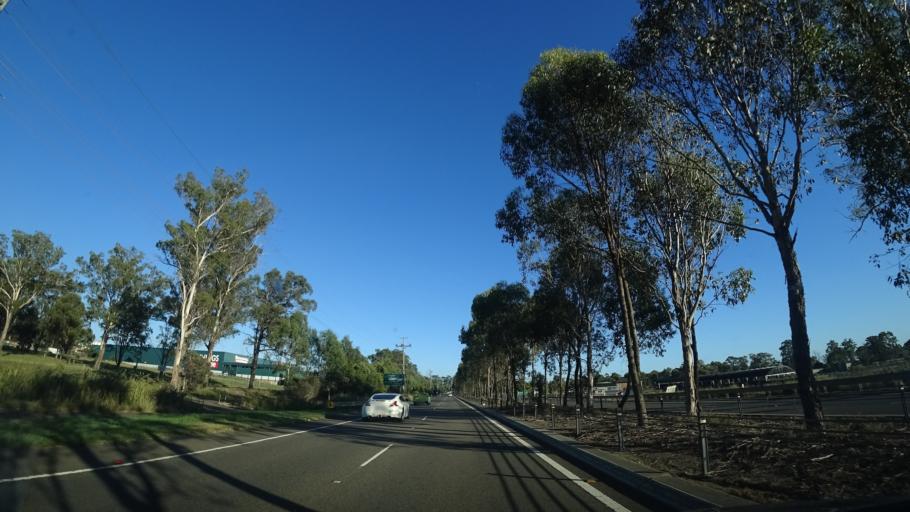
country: AU
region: New South Wales
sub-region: Hawkesbury
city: South Windsor
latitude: -33.6288
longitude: 150.8421
